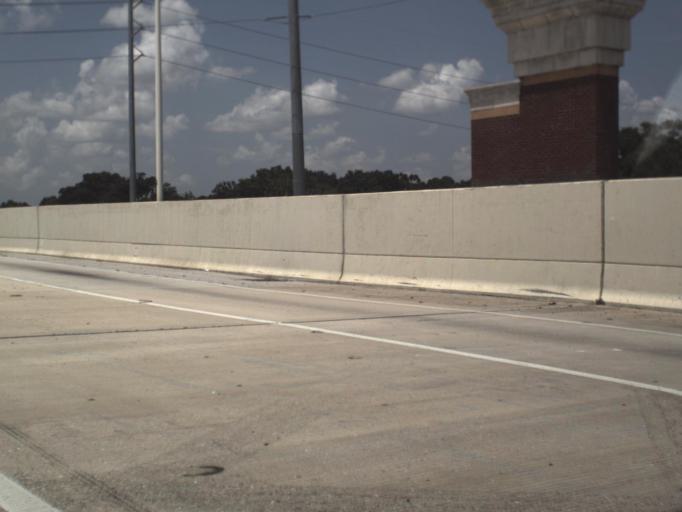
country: US
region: Florida
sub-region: Hillsborough County
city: Tampa
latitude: 27.9655
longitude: -82.4307
